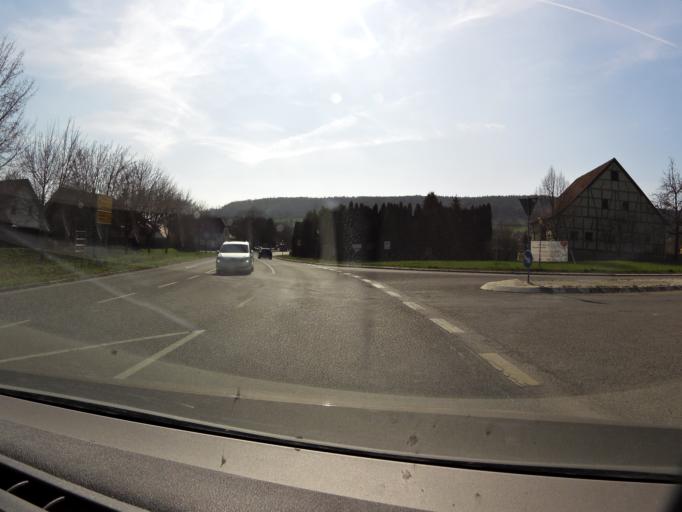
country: DE
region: Baden-Wuerttemberg
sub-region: Regierungsbezirk Stuttgart
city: Weikersheim
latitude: 49.4979
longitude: 9.9053
